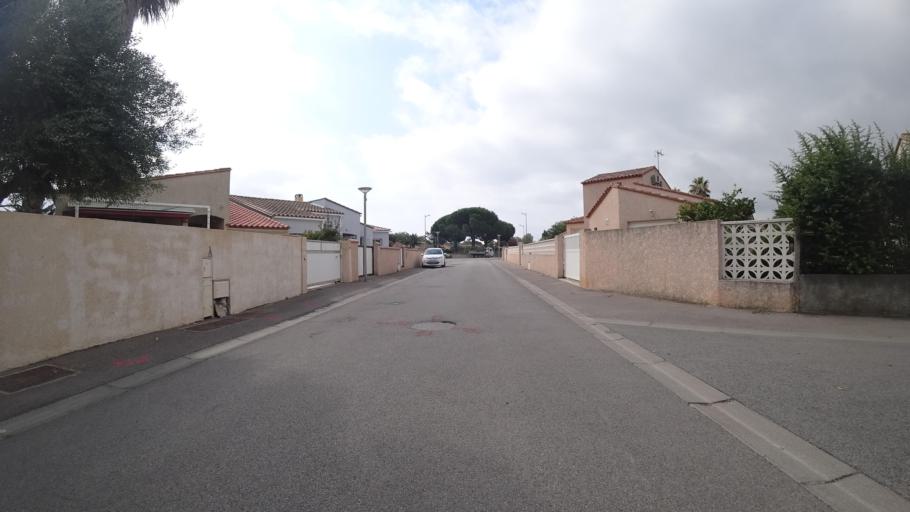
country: FR
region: Languedoc-Roussillon
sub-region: Departement des Pyrenees-Orientales
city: Sainte-Marie-Plage
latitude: 42.7348
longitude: 3.0287
